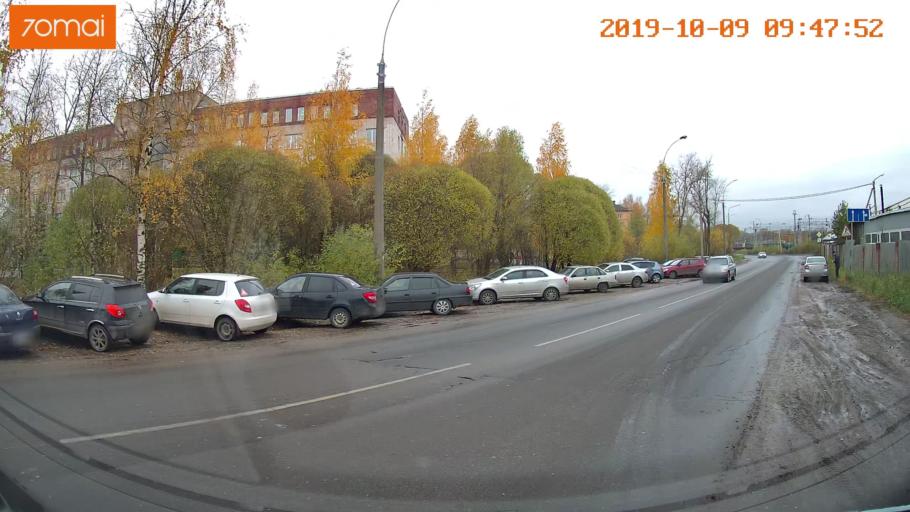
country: RU
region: Vologda
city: Vologda
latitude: 59.1921
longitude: 39.9346
